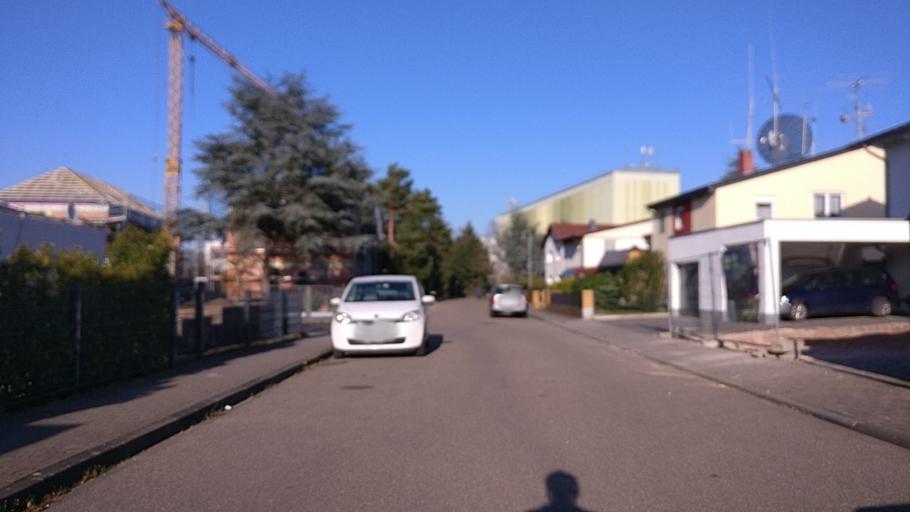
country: DE
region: Rheinland-Pfalz
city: Gau-Algesheim
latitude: 49.9704
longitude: 8.0341
